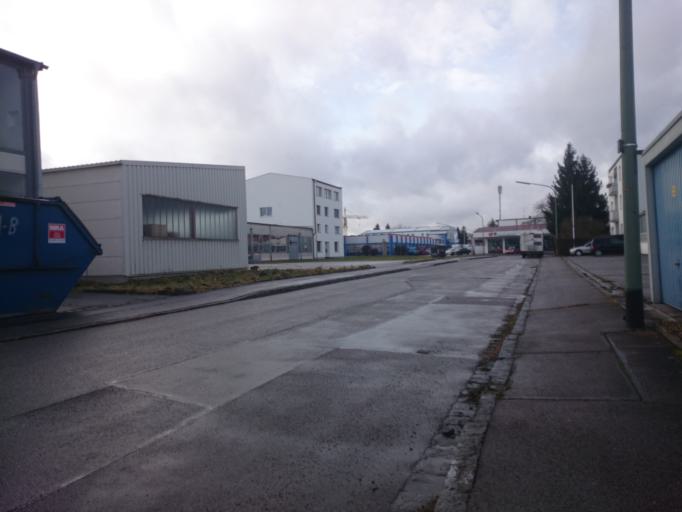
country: DE
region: Bavaria
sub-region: Swabia
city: Konigsbrunn
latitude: 48.2913
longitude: 10.8947
